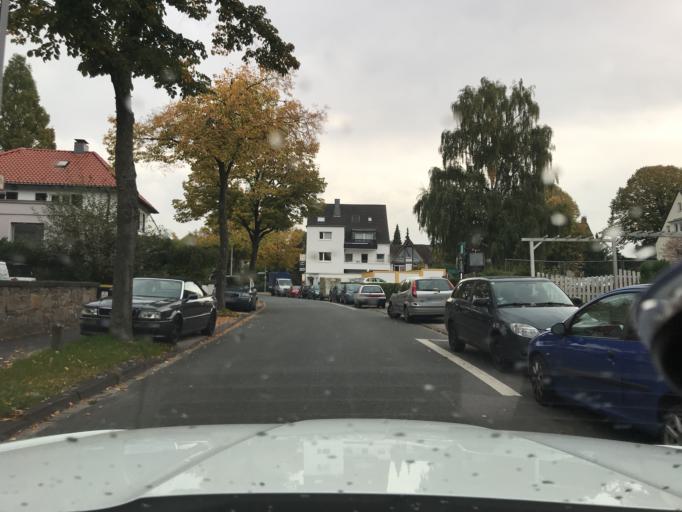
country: DE
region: North Rhine-Westphalia
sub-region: Regierungsbezirk Dusseldorf
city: Muelheim (Ruhr)
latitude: 51.4184
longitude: 6.8866
